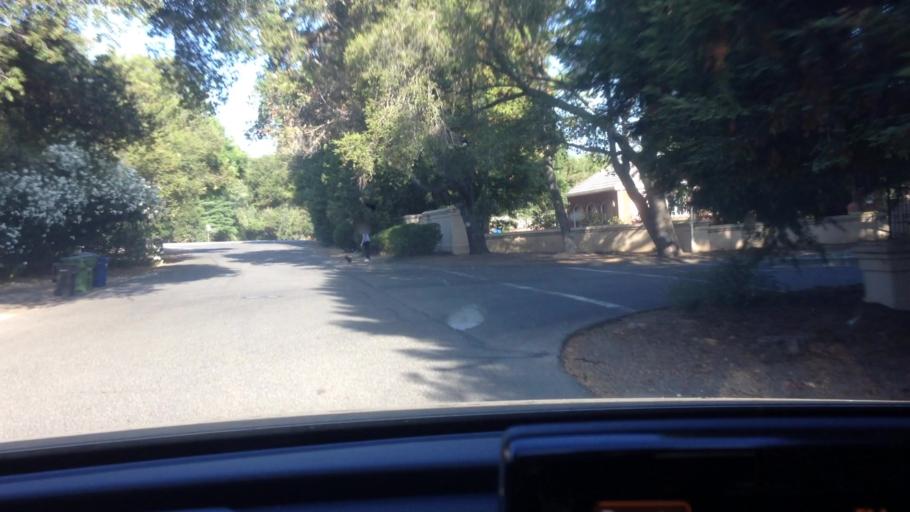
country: US
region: California
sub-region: Santa Clara County
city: Saratoga
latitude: 37.2503
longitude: -122.0188
